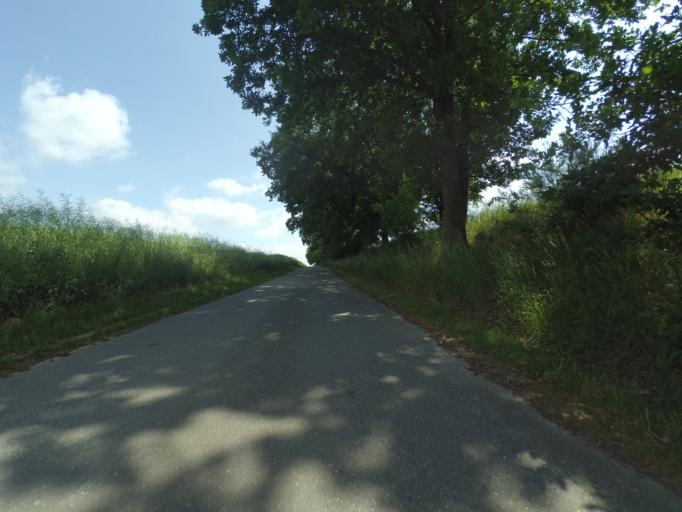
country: DE
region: Mecklenburg-Vorpommern
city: Neuburg
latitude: 53.4798
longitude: 11.9052
